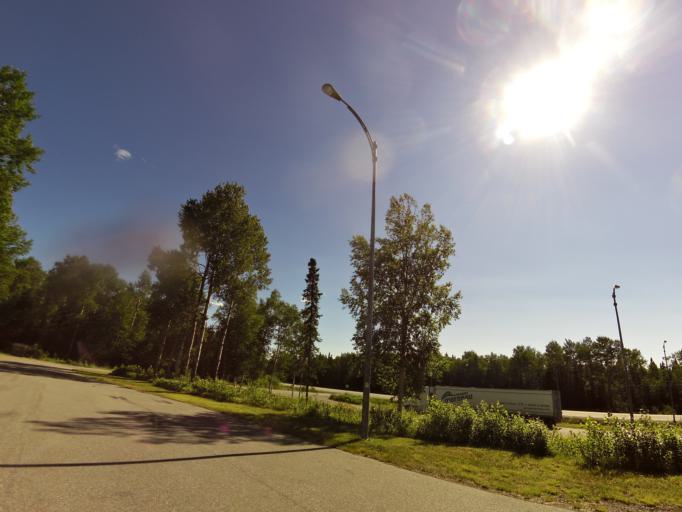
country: CA
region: Quebec
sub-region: Abitibi-Temiscamingue
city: Senneterre
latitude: 47.9985
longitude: -77.3596
